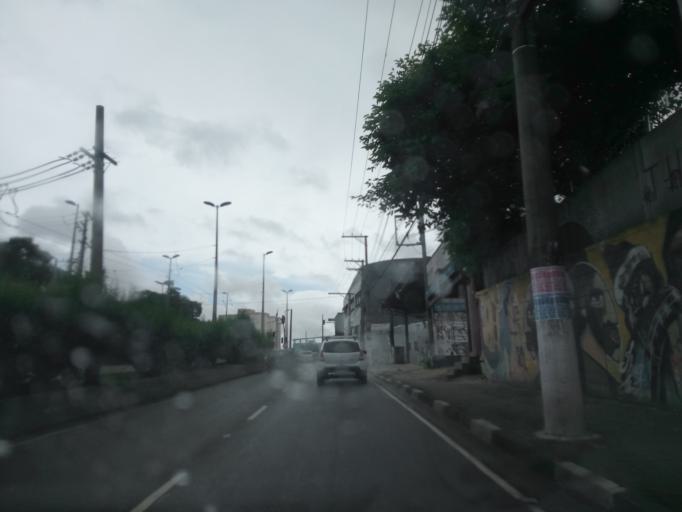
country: BR
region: Sao Paulo
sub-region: Sao Bernardo Do Campo
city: Sao Bernardo do Campo
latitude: -23.6866
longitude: -46.5928
